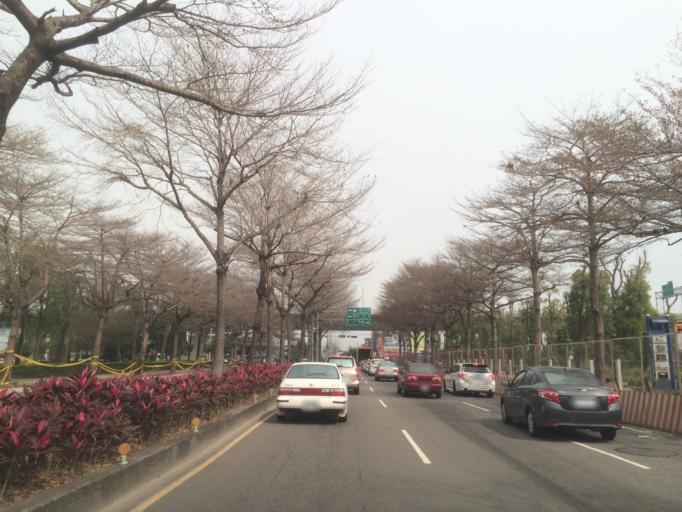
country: TW
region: Taiwan
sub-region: Taichung City
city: Taichung
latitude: 24.1996
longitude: 120.6866
